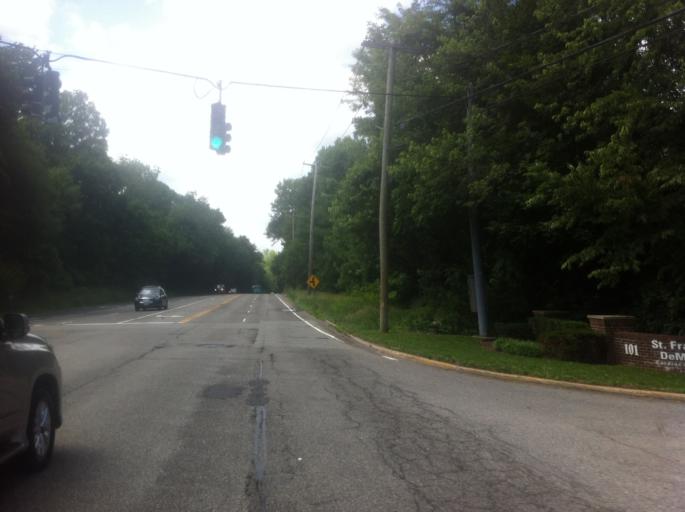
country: US
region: New York
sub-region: Nassau County
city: Old Brookville
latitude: 40.8169
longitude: -73.6071
